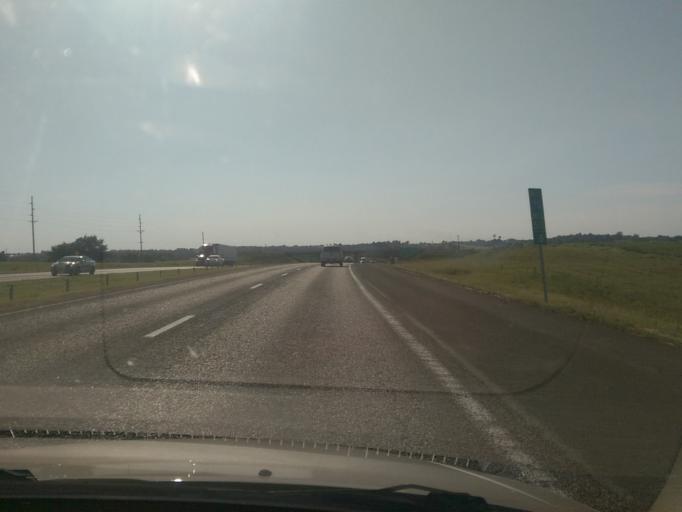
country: US
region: Missouri
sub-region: Lafayette County
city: Higginsville
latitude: 38.9932
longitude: -93.7082
